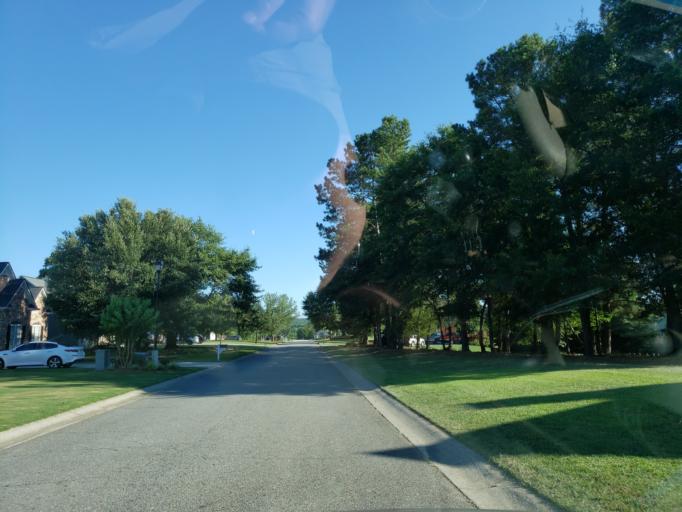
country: US
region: Georgia
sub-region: Bartow County
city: Euharlee
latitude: 34.1065
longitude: -84.9951
